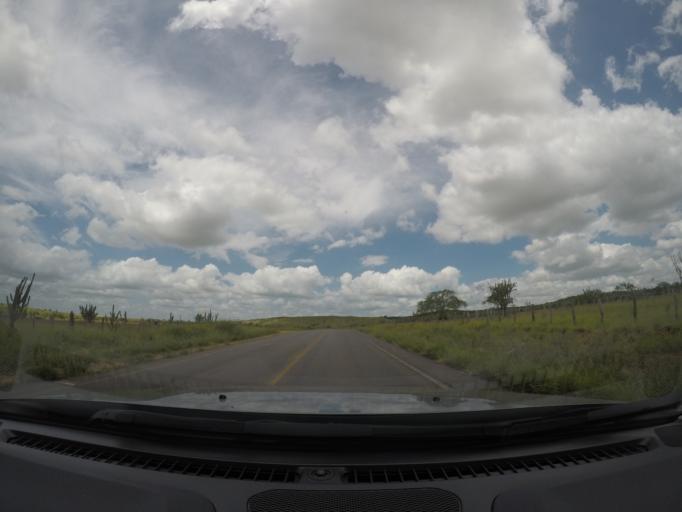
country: BR
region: Bahia
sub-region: Ipira
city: Ipira
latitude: -12.2584
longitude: -39.8248
